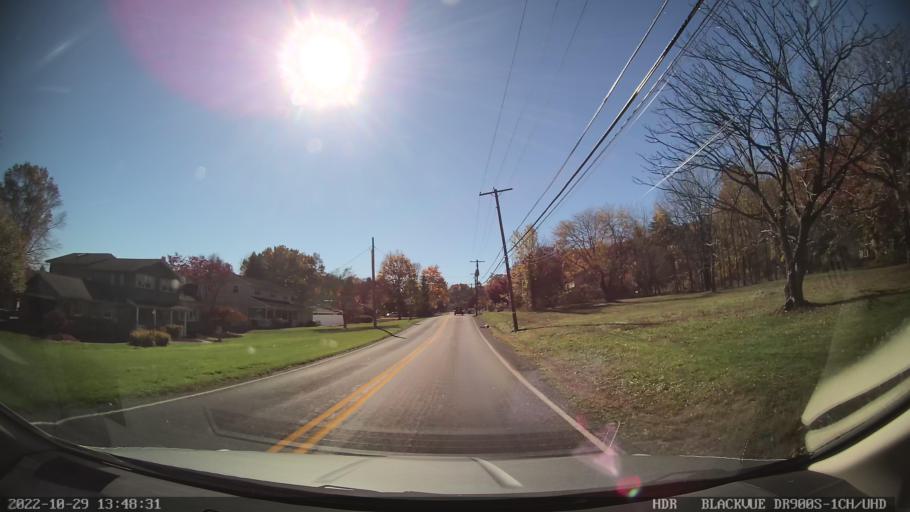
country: US
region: Pennsylvania
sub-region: Lehigh County
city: Emmaus
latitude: 40.5479
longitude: -75.4511
